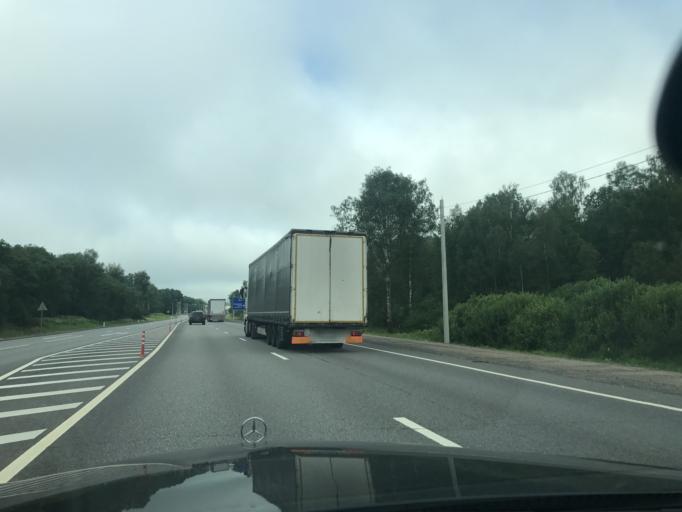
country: RU
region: Smolensk
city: Vyaz'ma
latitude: 55.2688
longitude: 34.3988
